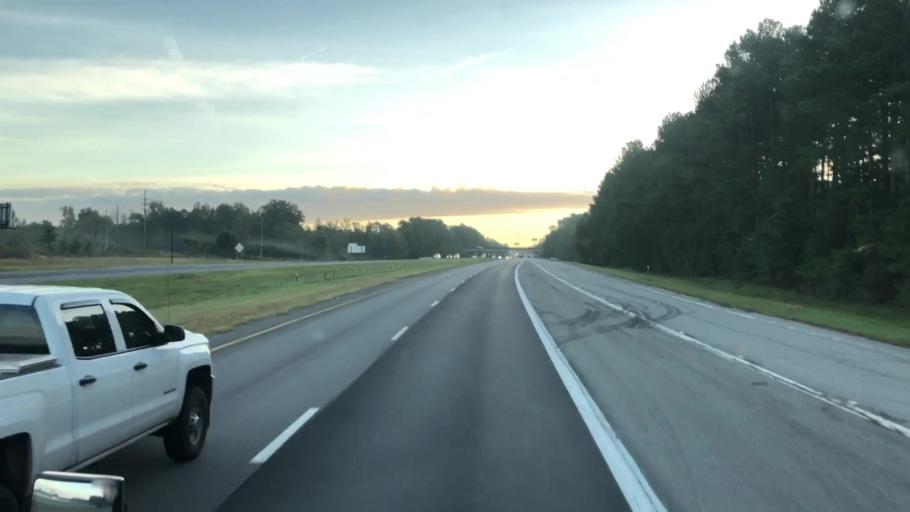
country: US
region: South Carolina
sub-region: Clarendon County
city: Manning
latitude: 33.5906
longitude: -80.3532
